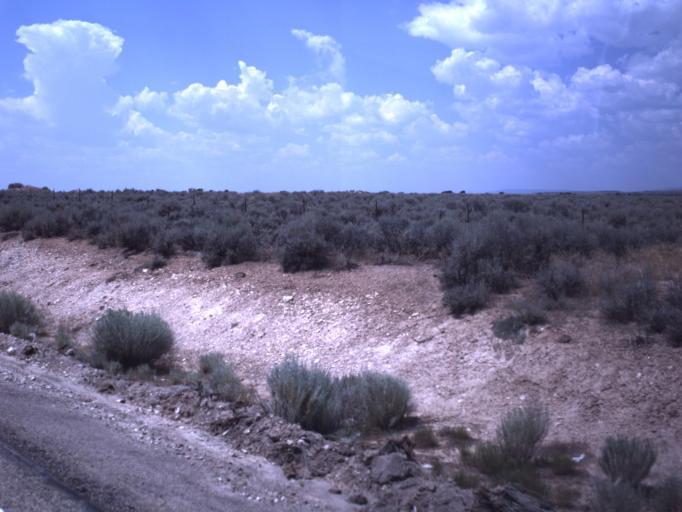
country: US
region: Utah
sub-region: Uintah County
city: Maeser
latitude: 40.4296
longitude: -109.6621
